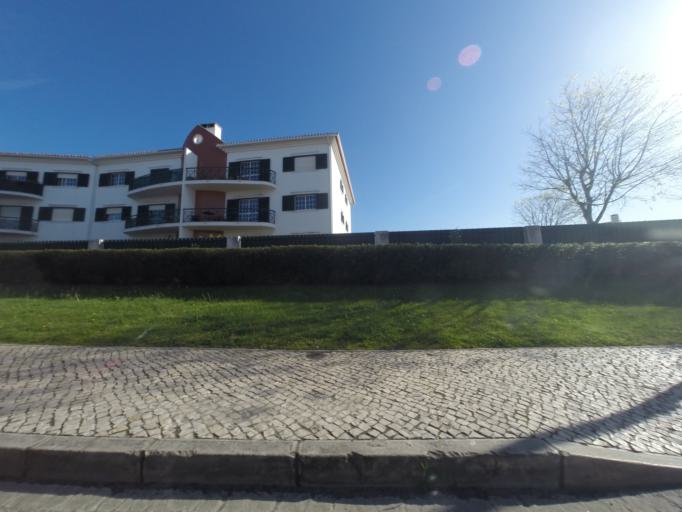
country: PT
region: Lisbon
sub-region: Oeiras
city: Paco de Arcos
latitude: 38.7037
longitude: -9.3005
